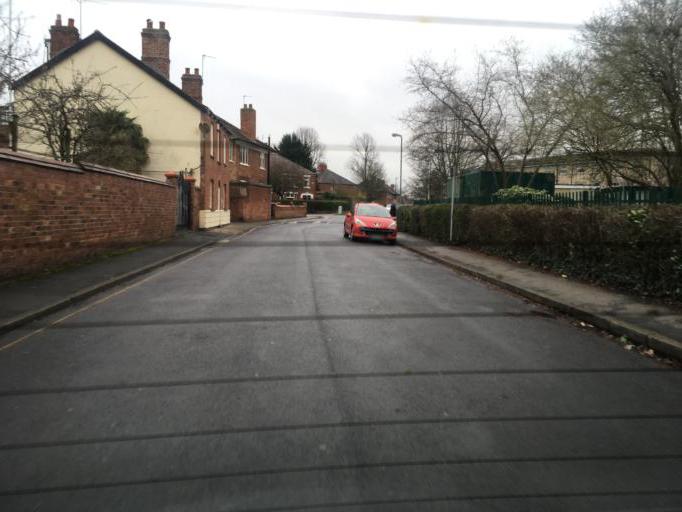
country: GB
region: England
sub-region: City of York
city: York
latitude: 53.9651
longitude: -1.0636
